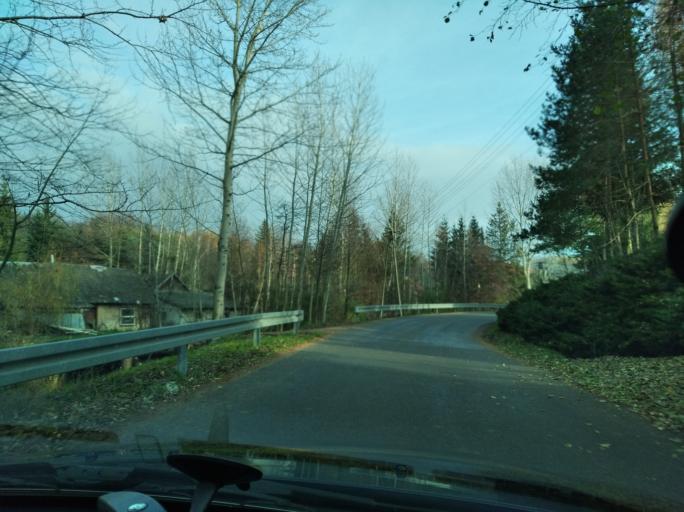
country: PL
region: Subcarpathian Voivodeship
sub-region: Powiat przeworski
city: Siedleczka
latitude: 49.9639
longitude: 22.3756
